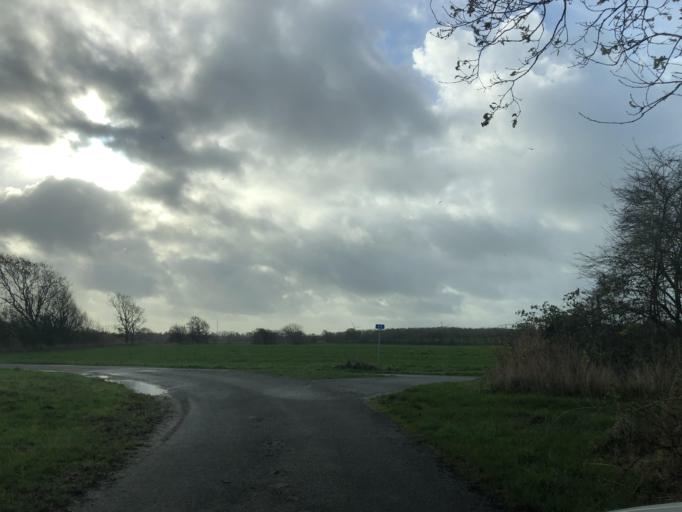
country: DK
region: South Denmark
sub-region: Esbjerg Kommune
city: Bramming
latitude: 55.4262
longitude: 8.7069
